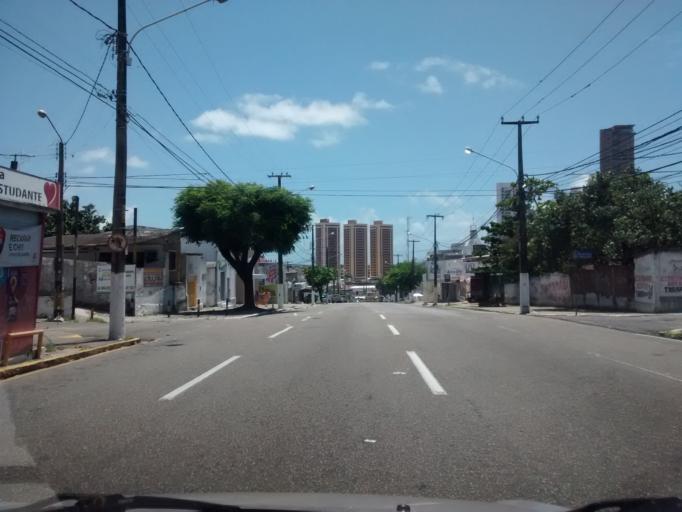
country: BR
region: Rio Grande do Norte
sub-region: Natal
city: Natal
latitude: -5.7837
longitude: -35.2057
